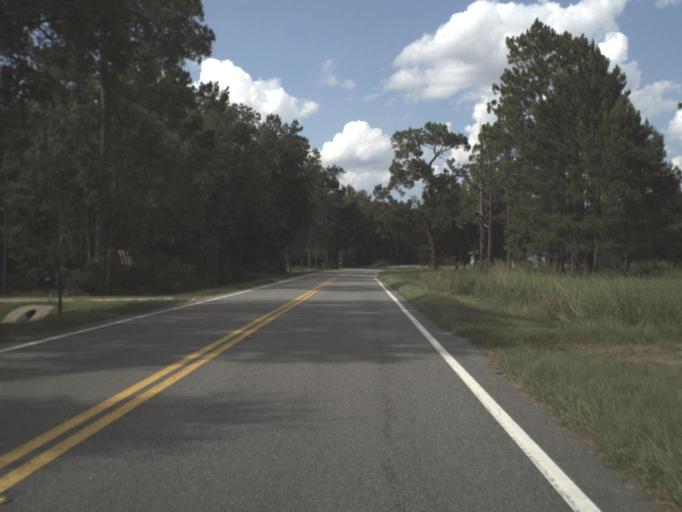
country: US
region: Florida
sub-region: Madison County
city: Madison
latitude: 30.4161
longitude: -83.6381
